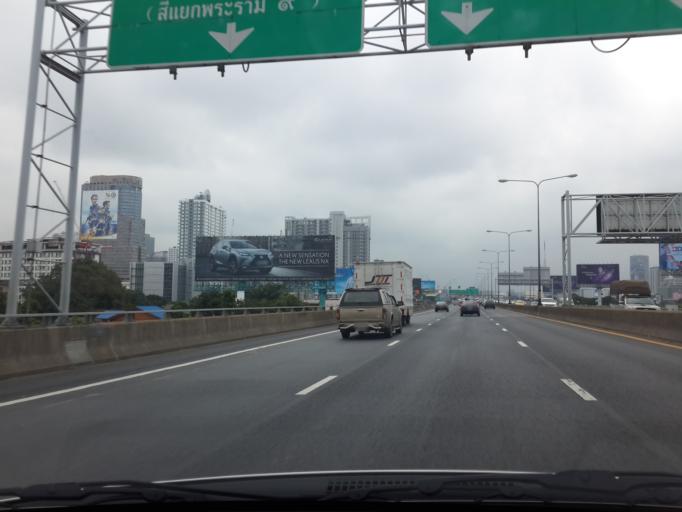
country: TH
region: Bangkok
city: Din Daeng
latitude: 13.7550
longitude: 100.5559
